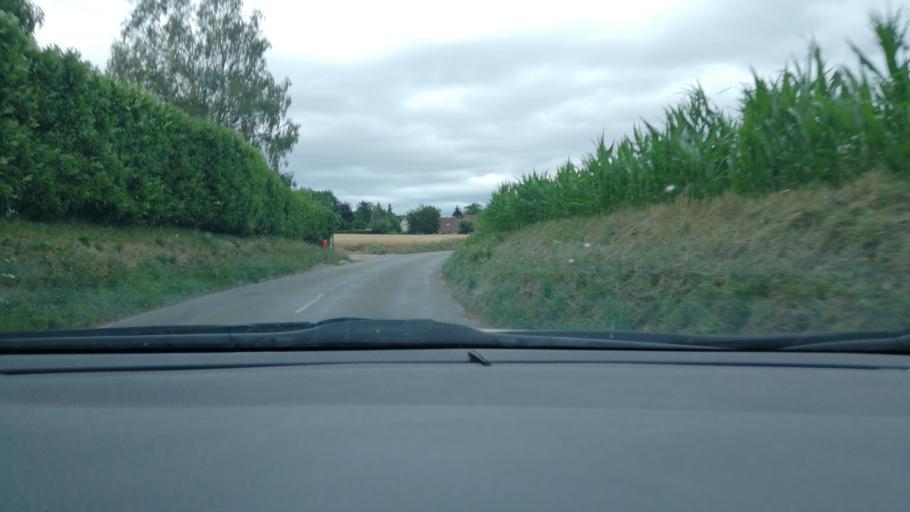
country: FR
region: Ile-de-France
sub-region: Departement du Val-d'Oise
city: Ennery
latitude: 49.0944
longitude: 2.0896
